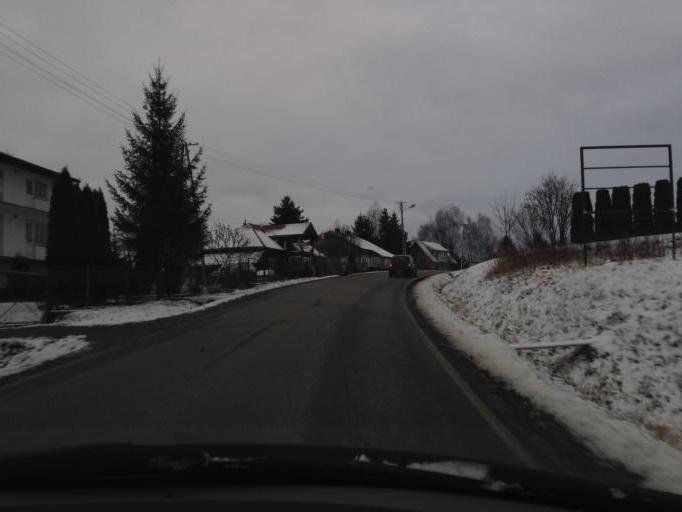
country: PL
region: Lesser Poland Voivodeship
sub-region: Powiat gorlicki
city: Moszczenica
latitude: 49.7399
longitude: 21.0880
